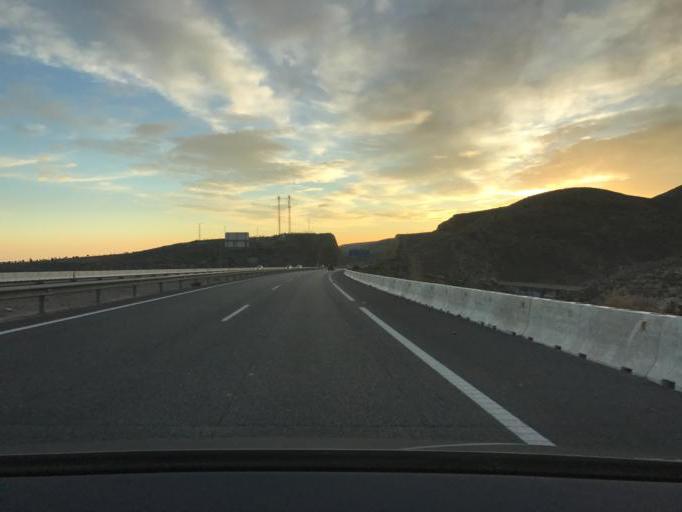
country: ES
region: Andalusia
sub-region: Provincia de Almeria
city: Almeria
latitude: 36.8639
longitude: -2.4655
